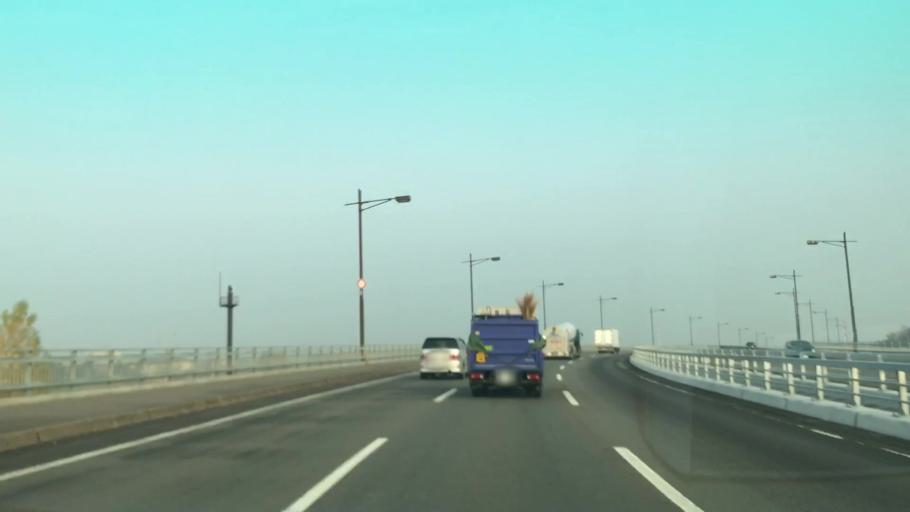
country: JP
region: Hokkaido
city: Ishikari
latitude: 43.1664
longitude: 141.3489
